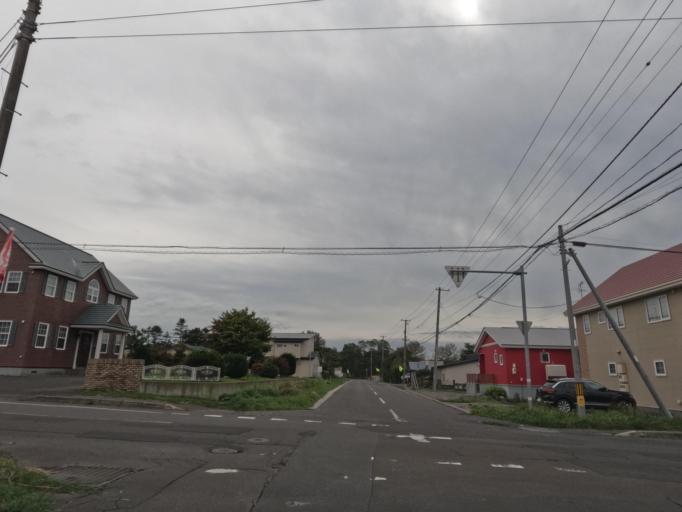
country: JP
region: Hokkaido
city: Date
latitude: 42.4302
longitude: 140.9111
